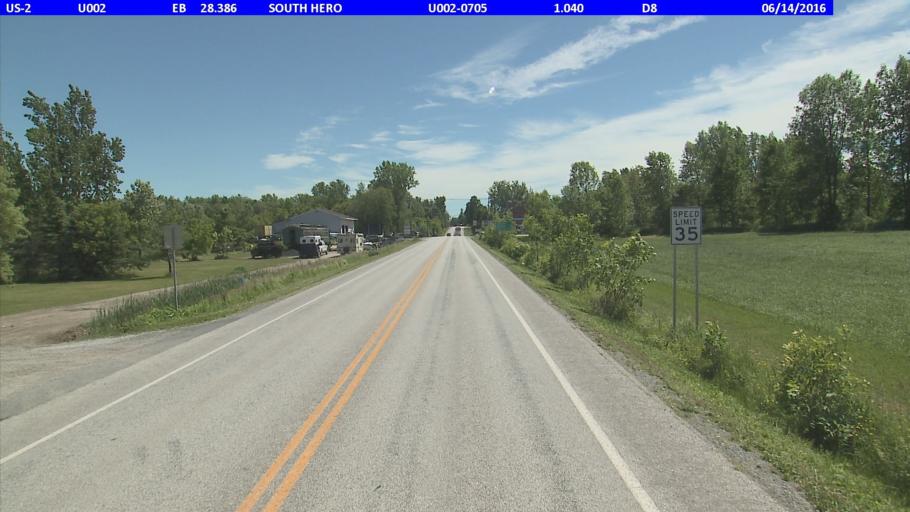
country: US
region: New York
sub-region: Clinton County
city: Cumberland Head
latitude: 44.6661
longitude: -73.3228
